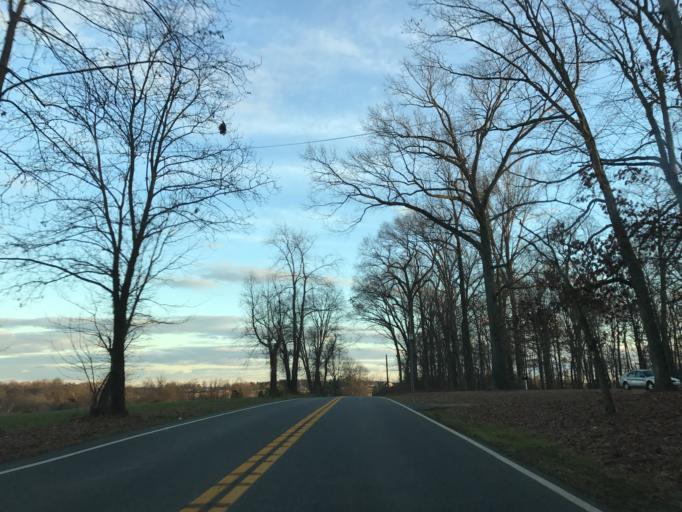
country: US
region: Pennsylvania
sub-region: York County
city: Susquehanna Trails
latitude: 39.7141
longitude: -76.2713
